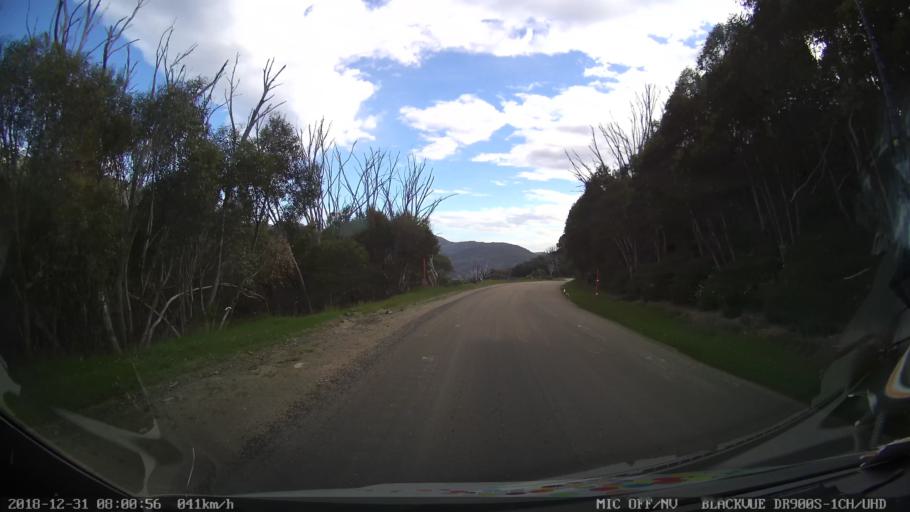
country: AU
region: New South Wales
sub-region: Snowy River
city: Jindabyne
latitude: -36.3660
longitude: 148.3939
